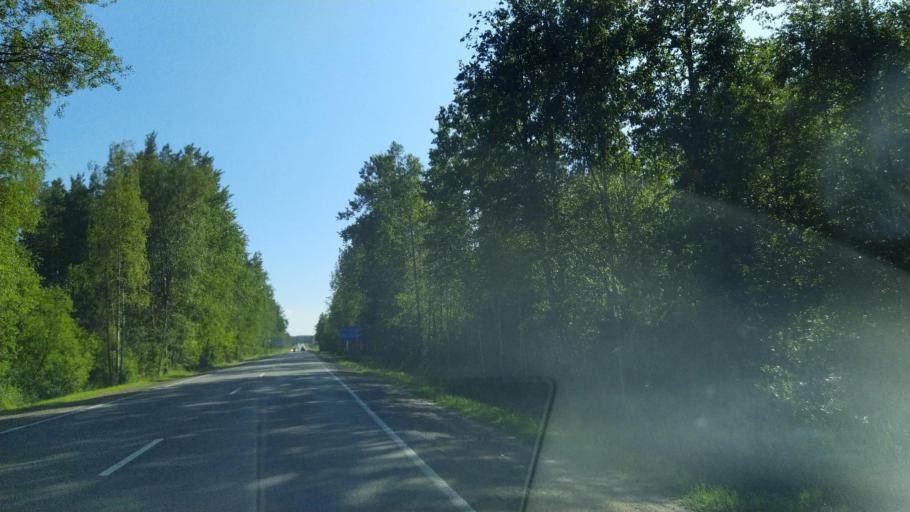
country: RU
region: Leningrad
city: Kirovsk
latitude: 59.9192
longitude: 30.9419
